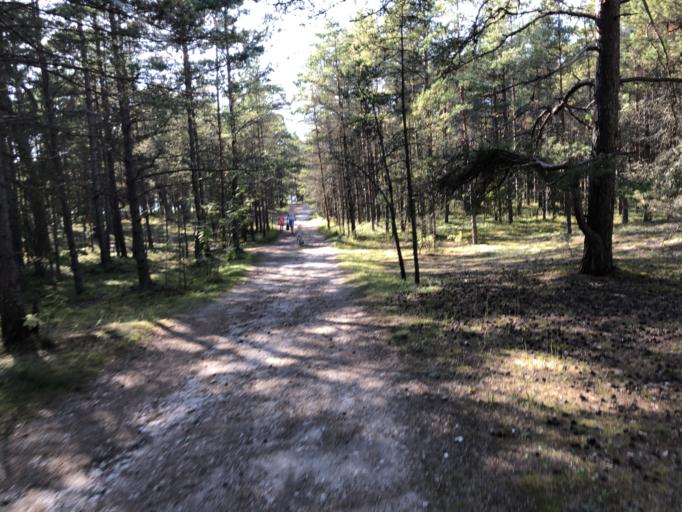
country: EE
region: Harju
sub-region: Keila linn
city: Keila
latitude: 59.3710
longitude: 24.2410
